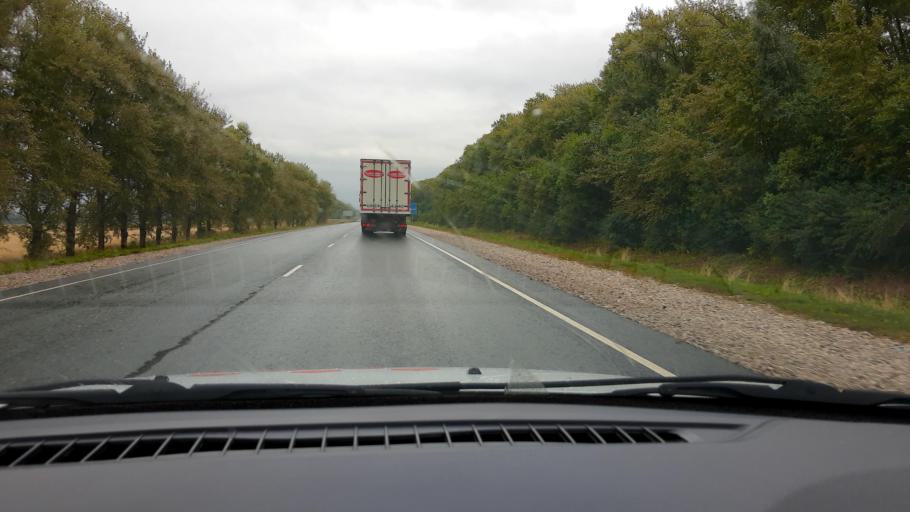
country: RU
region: Chuvashia
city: Yantikovo
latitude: 55.7892
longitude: 47.7193
